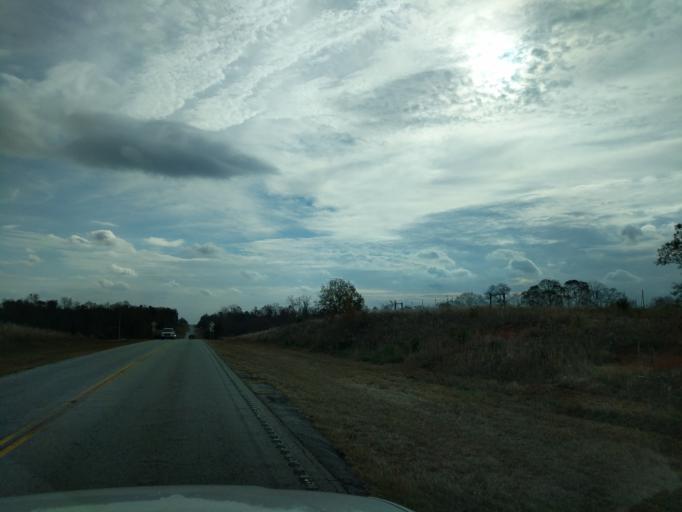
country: US
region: South Carolina
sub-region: Oconee County
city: Westminster
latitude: 34.6117
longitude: -83.0461
